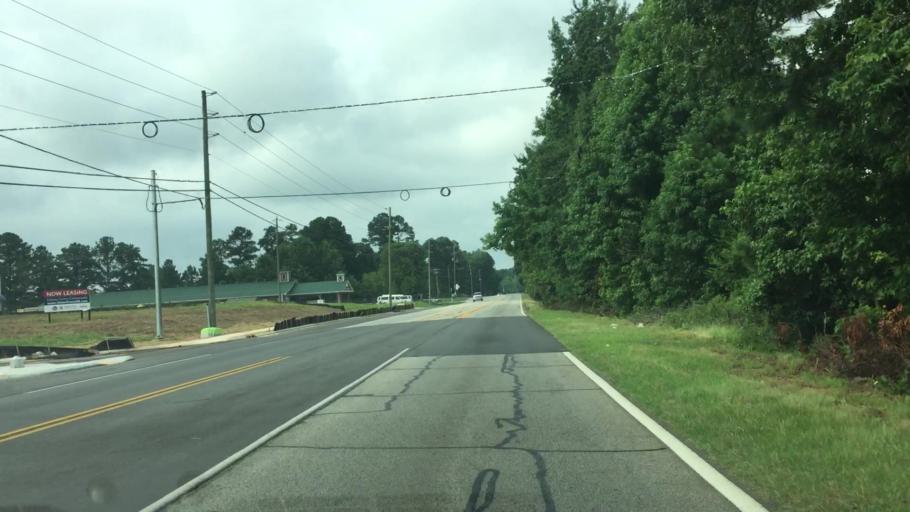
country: US
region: Georgia
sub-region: Henry County
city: McDonough
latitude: 33.5051
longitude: -84.1422
